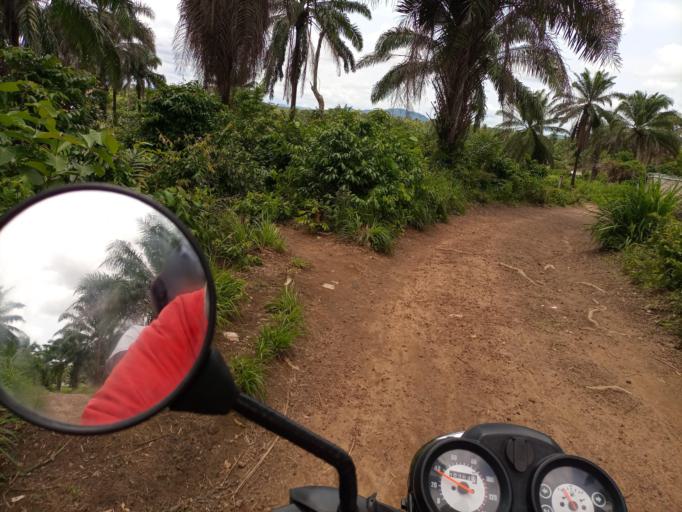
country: SL
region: Southern Province
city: Baoma
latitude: 7.9796
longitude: -11.7135
